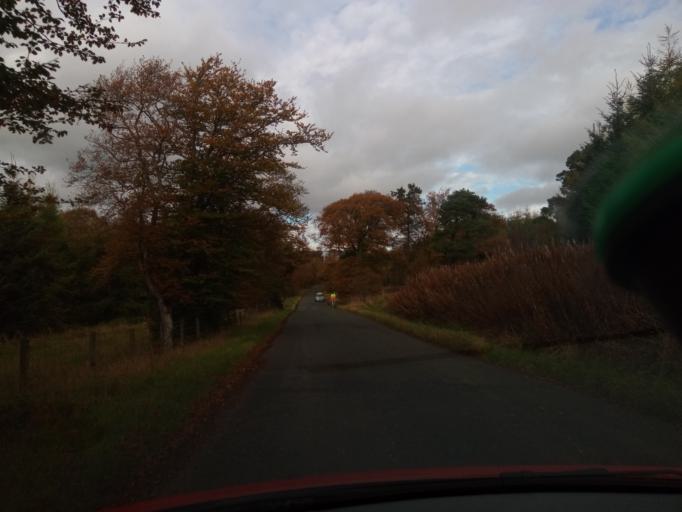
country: GB
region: Scotland
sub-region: South Lanarkshire
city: Carnwath
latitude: 55.7403
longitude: -3.6033
